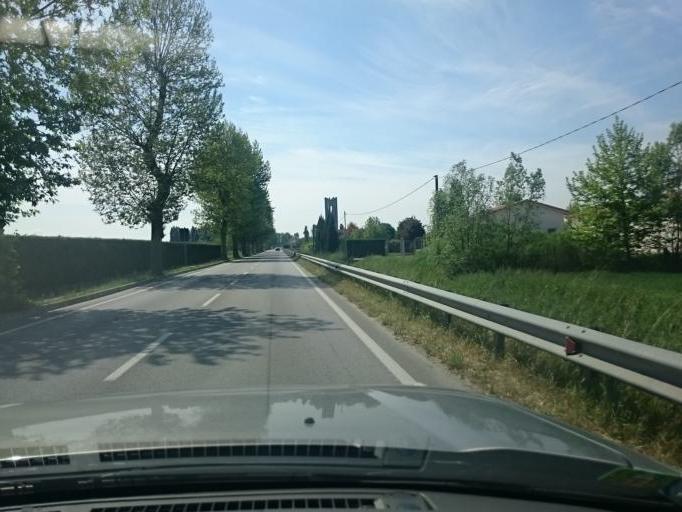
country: IT
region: Veneto
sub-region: Provincia di Padova
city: Masera di Padova
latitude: 45.2928
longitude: 11.8695
